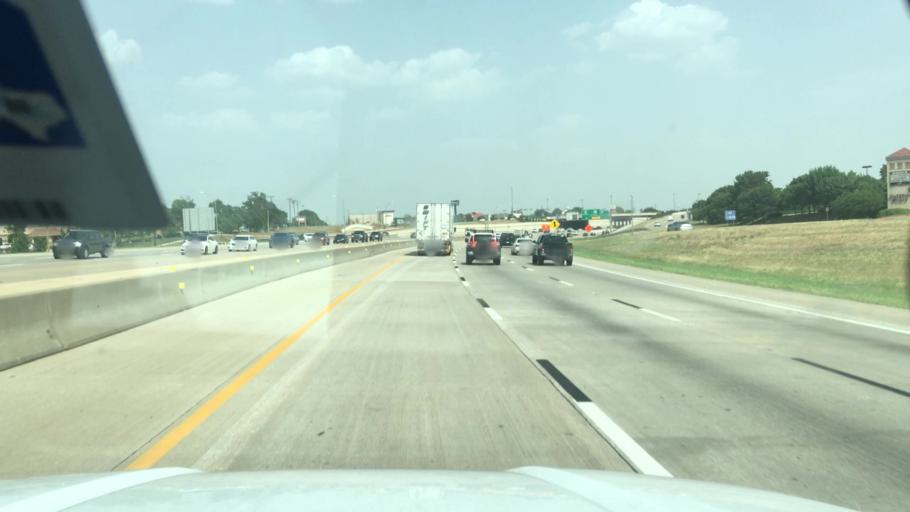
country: US
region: Texas
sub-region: Tarrant County
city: Southlake
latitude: 32.9423
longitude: -97.1056
